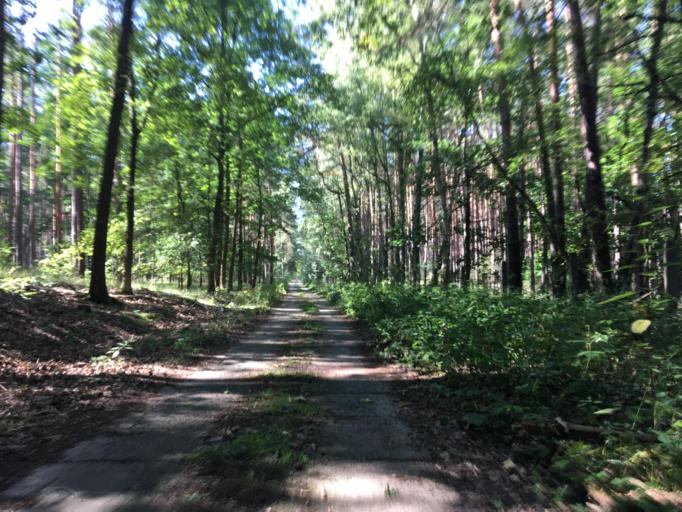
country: DE
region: Brandenburg
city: Gross Koris
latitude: 52.1947
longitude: 13.7270
